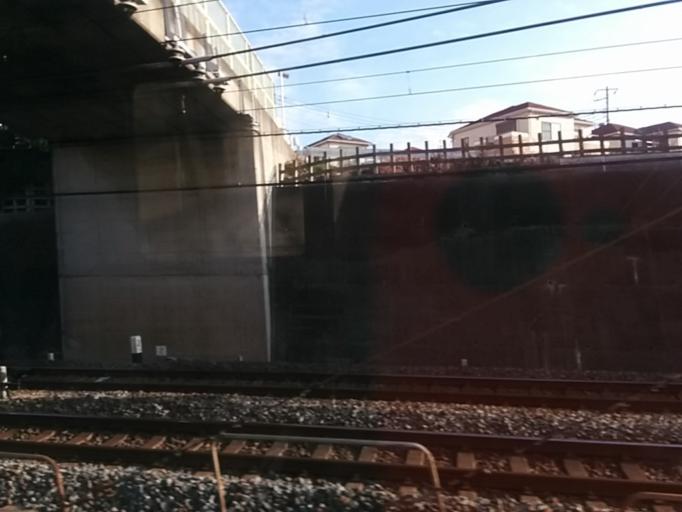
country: JP
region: Saitama
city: Asaka
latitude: 35.8068
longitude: 139.5967
